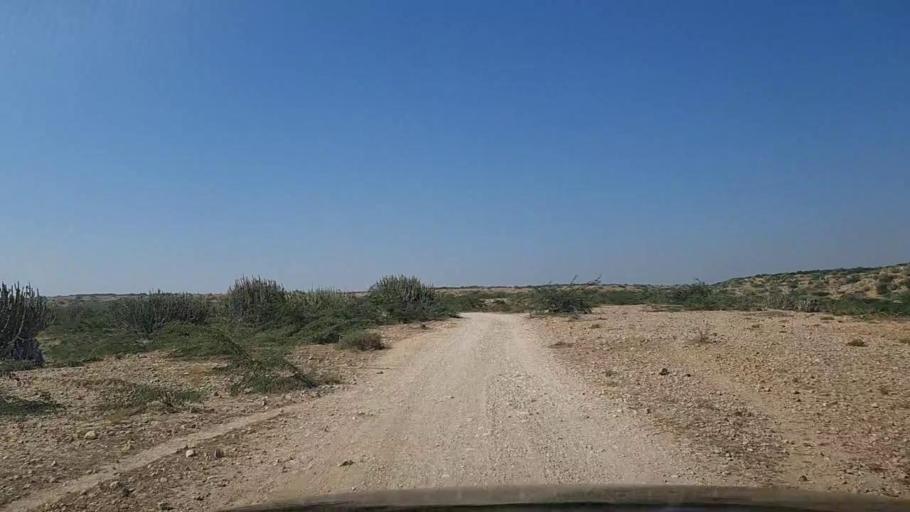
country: PK
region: Sindh
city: Thatta
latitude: 24.6284
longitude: 67.8624
